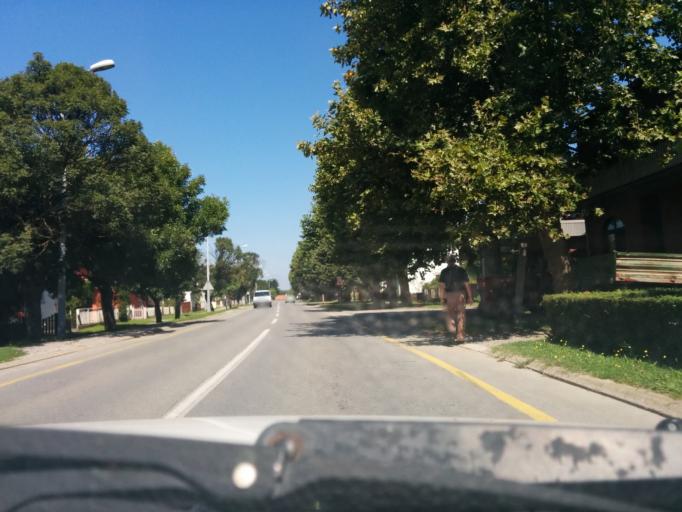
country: HR
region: Sisacko-Moslavacka
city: Novska
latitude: 45.3466
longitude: 16.9724
